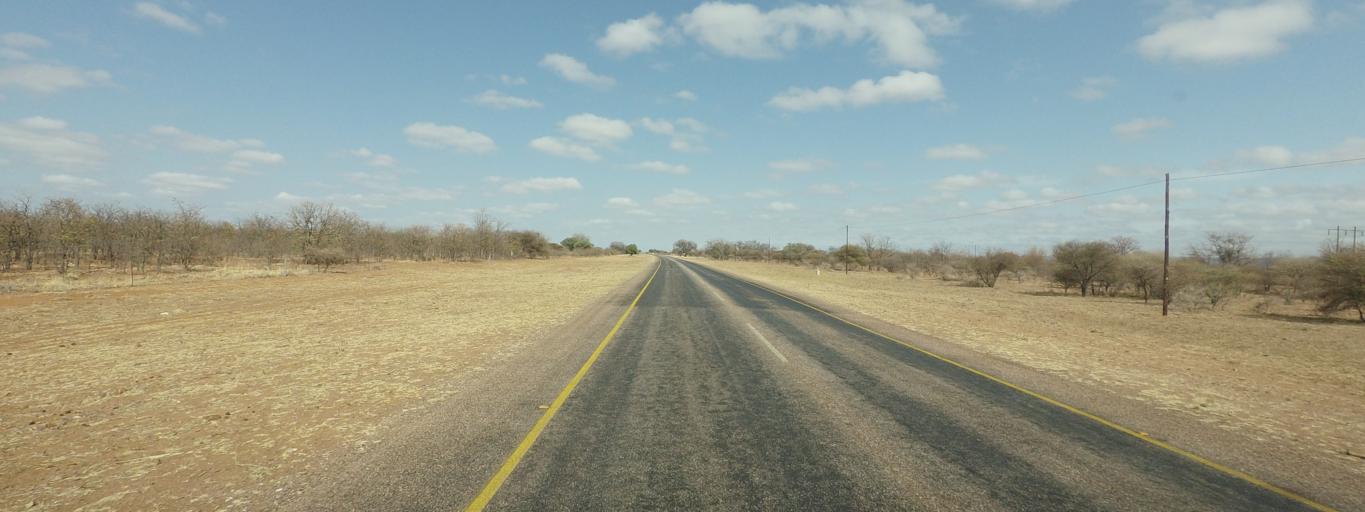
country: BW
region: Central
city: Ratholo
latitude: -22.8028
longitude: 27.5084
